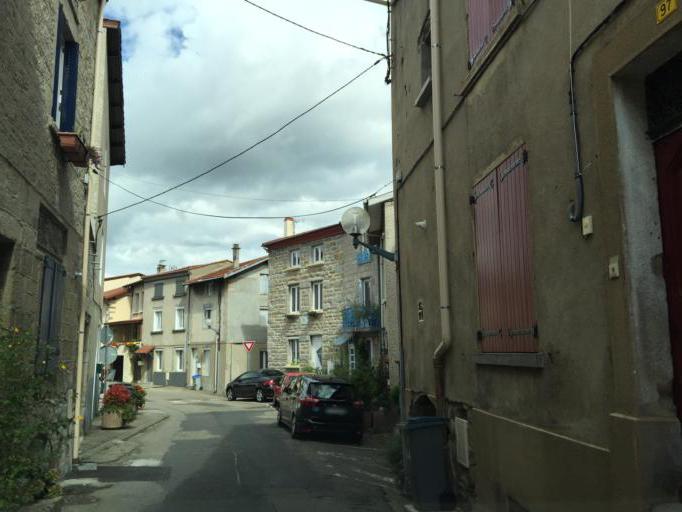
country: FR
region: Rhone-Alpes
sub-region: Departement de la Loire
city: Saint-Martin-la-Plaine
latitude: 45.5309
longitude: 4.5815
